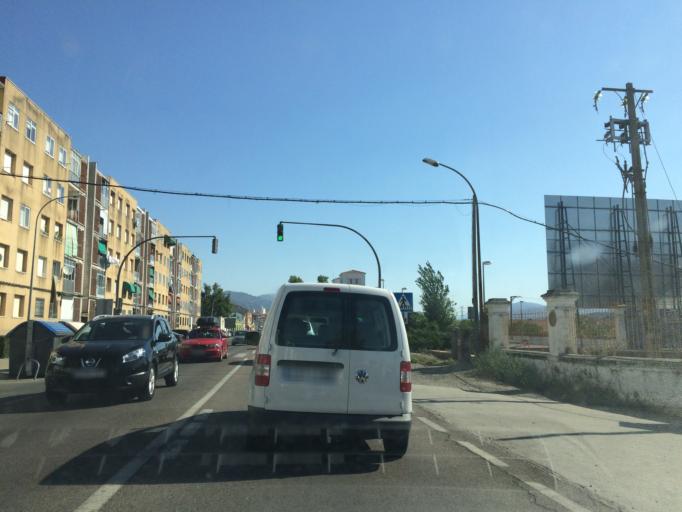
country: ES
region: Extremadura
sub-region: Provincia de Caceres
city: Plasencia
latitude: 40.0180
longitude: -6.1015
